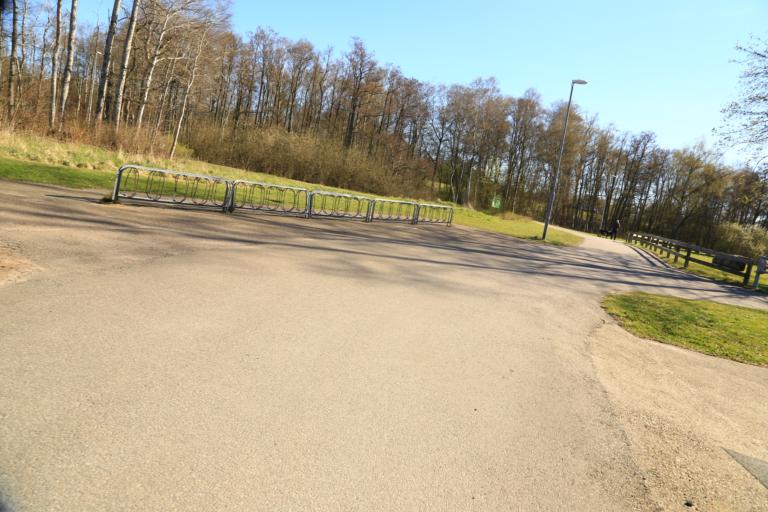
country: SE
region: Halland
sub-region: Varbergs Kommun
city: Varberg
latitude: 57.1186
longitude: 12.2781
